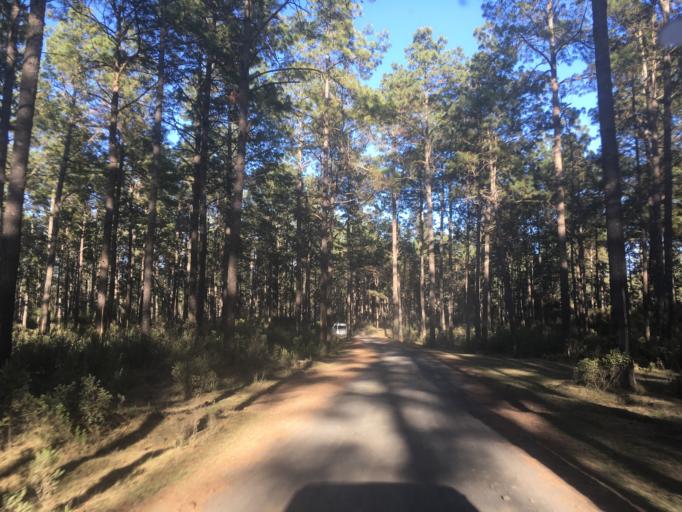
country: MX
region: Michoacan
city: Angahuan
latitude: 19.4636
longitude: -102.2293
